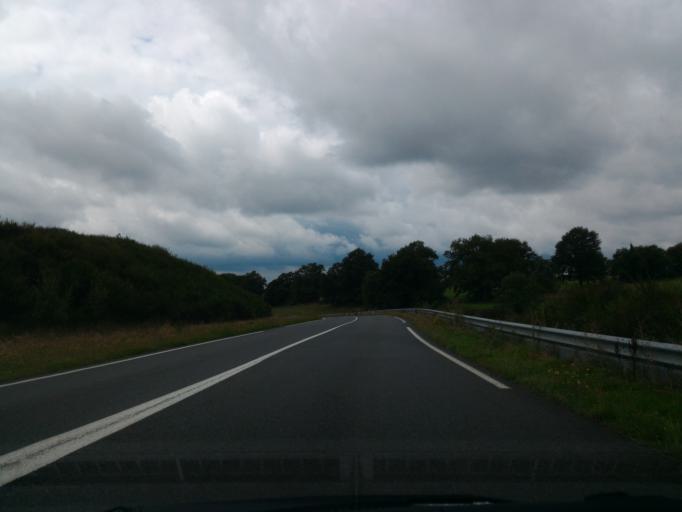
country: FR
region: Poitou-Charentes
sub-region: Departement de la Charente
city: Etagnac
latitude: 45.8810
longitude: 0.7529
